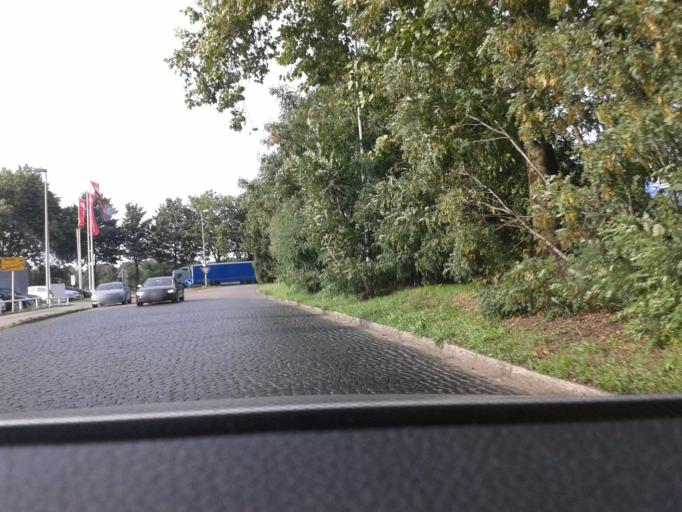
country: DE
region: North Rhine-Westphalia
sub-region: Regierungsbezirk Dusseldorf
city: Duisburg
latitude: 51.4431
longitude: 6.7618
